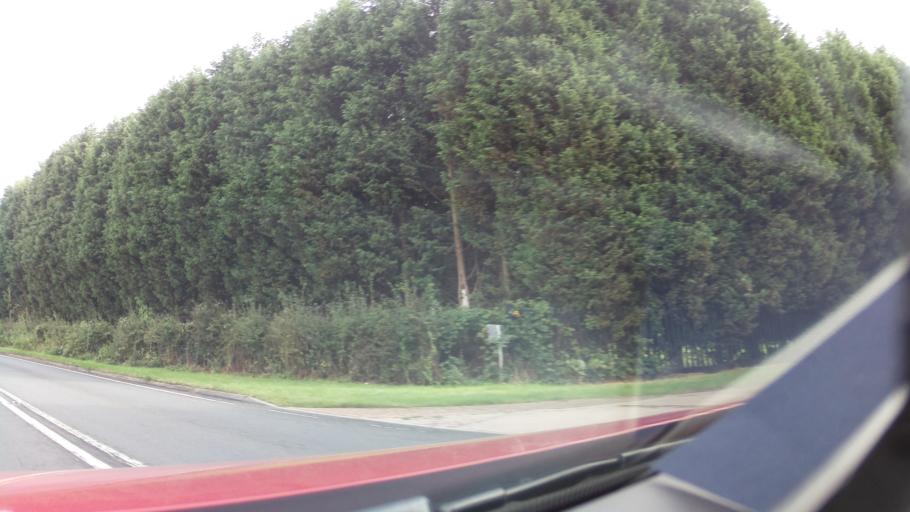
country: GB
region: England
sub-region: Worcestershire
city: Kidderminster
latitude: 52.3749
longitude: -2.2209
